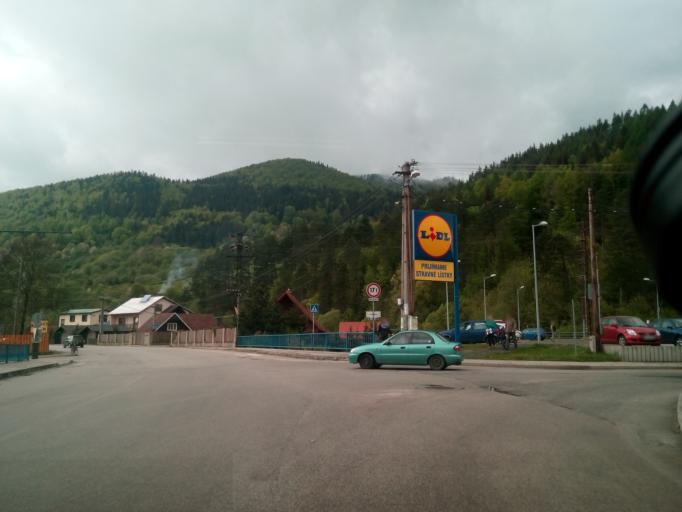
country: SK
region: Zilinsky
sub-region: Okres Zilina
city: Terchova
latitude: 49.2586
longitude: 19.0291
